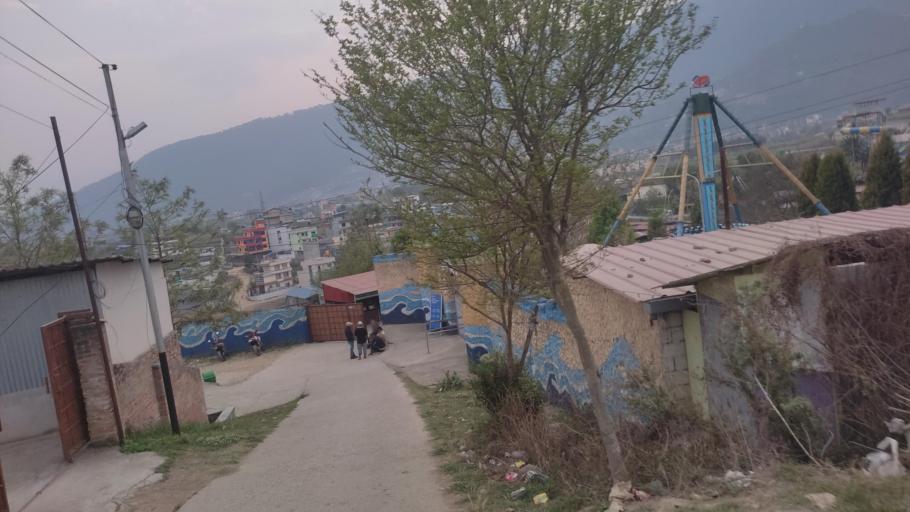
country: NP
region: Central Region
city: Kirtipur
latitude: 27.6623
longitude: 85.2878
